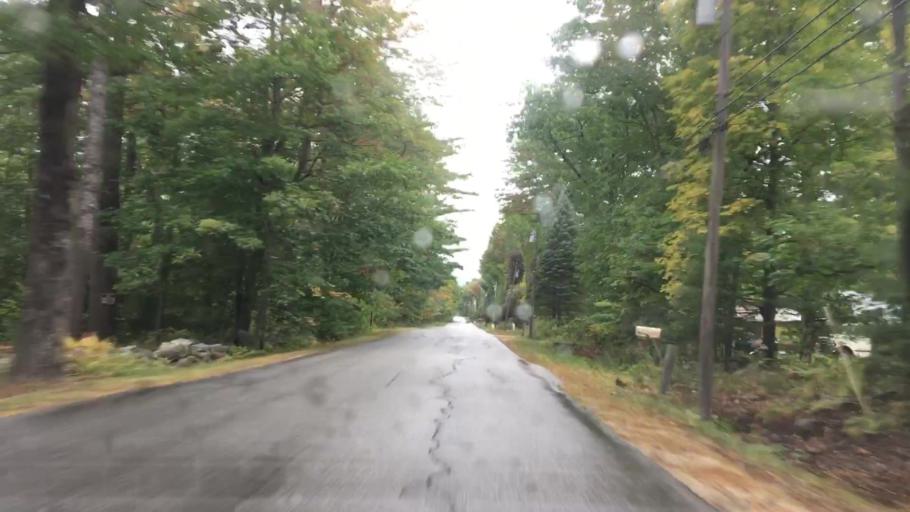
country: US
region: Maine
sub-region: Cumberland County
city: Harrison
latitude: 44.0719
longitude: -70.6353
